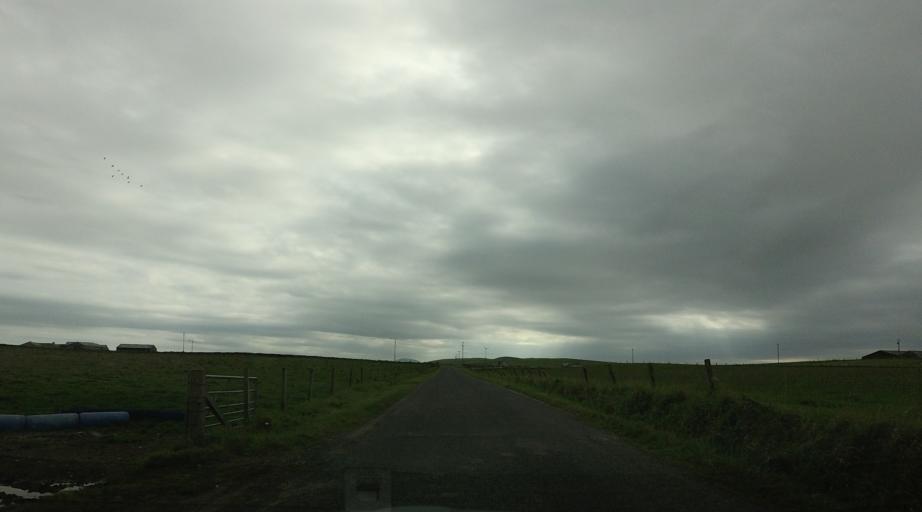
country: GB
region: Scotland
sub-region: Orkney Islands
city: Stromness
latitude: 59.0382
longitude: -3.3113
